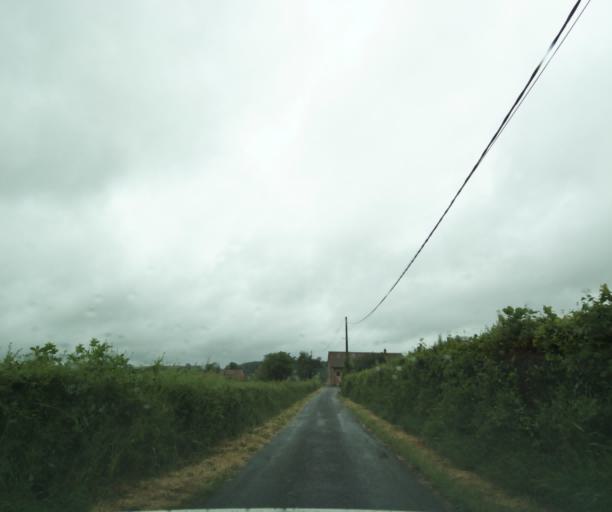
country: FR
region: Bourgogne
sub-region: Departement de Saone-et-Loire
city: Charolles
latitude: 46.4822
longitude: 4.4127
